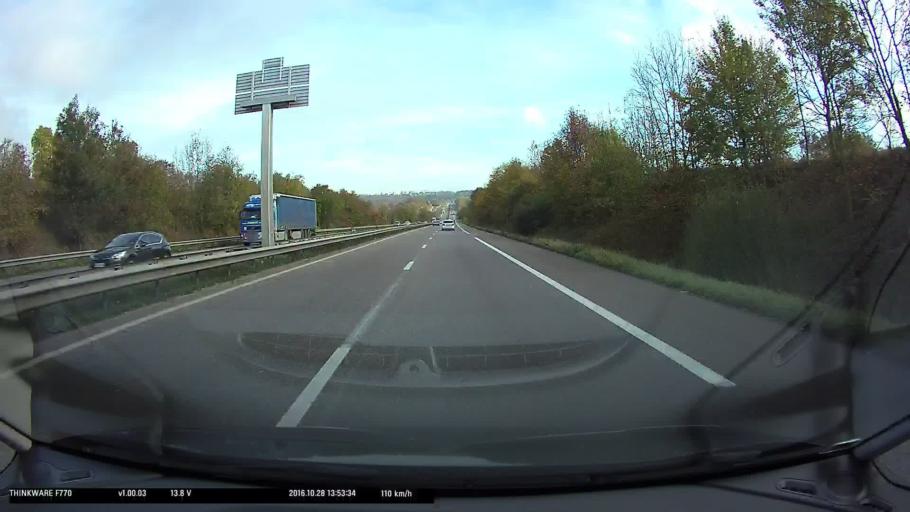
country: FR
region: Lorraine
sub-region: Departement de Meurthe-et-Moselle
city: Velaine-en-Haye
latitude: 48.6935
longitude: 6.0792
